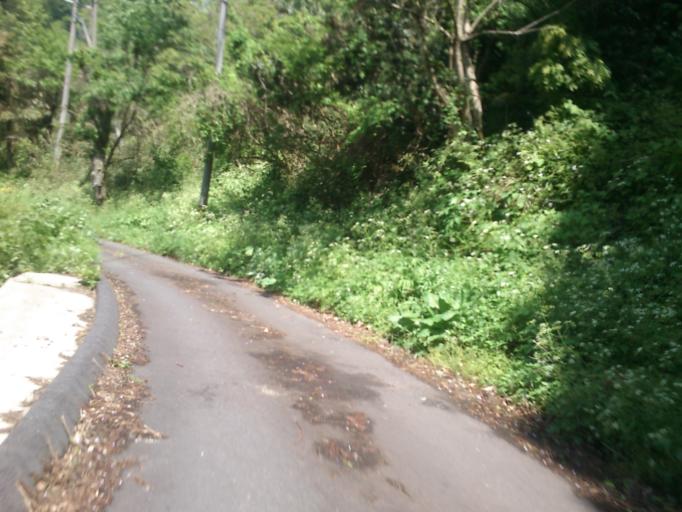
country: JP
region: Kyoto
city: Miyazu
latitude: 35.7155
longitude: 135.1661
